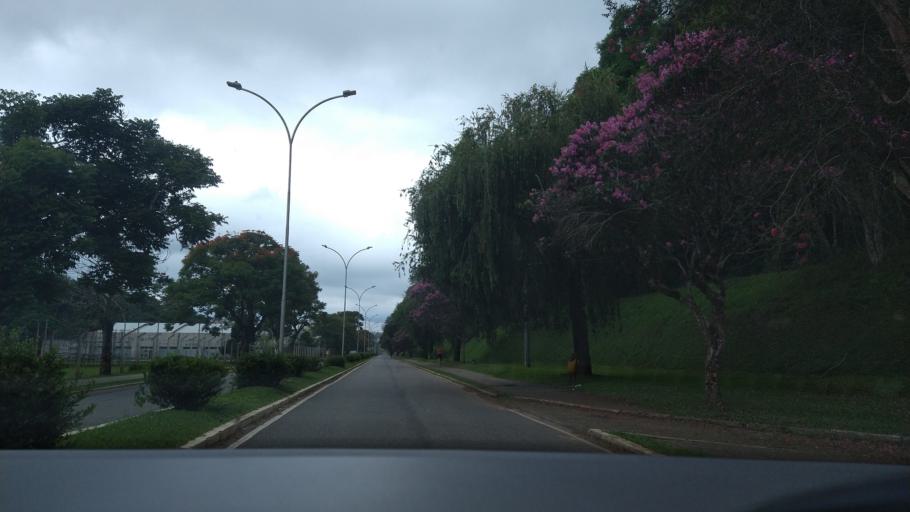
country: BR
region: Minas Gerais
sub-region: Vicosa
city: Vicosa
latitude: -20.7655
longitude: -42.8634
